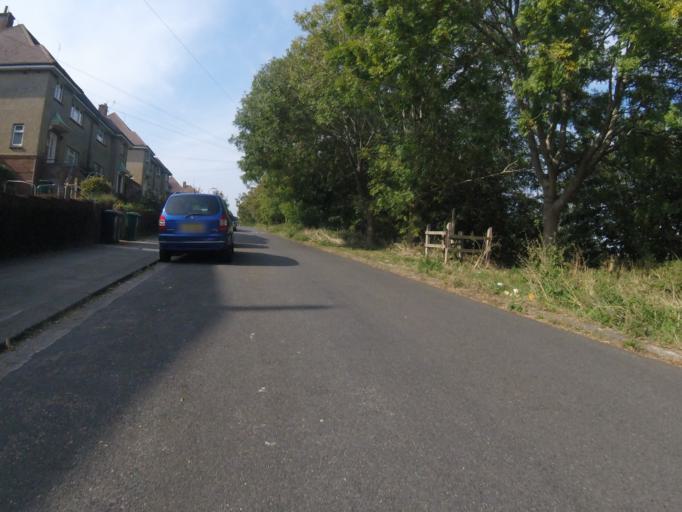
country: GB
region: England
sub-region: Brighton and Hove
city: Hove
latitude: 50.8495
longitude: -0.1843
